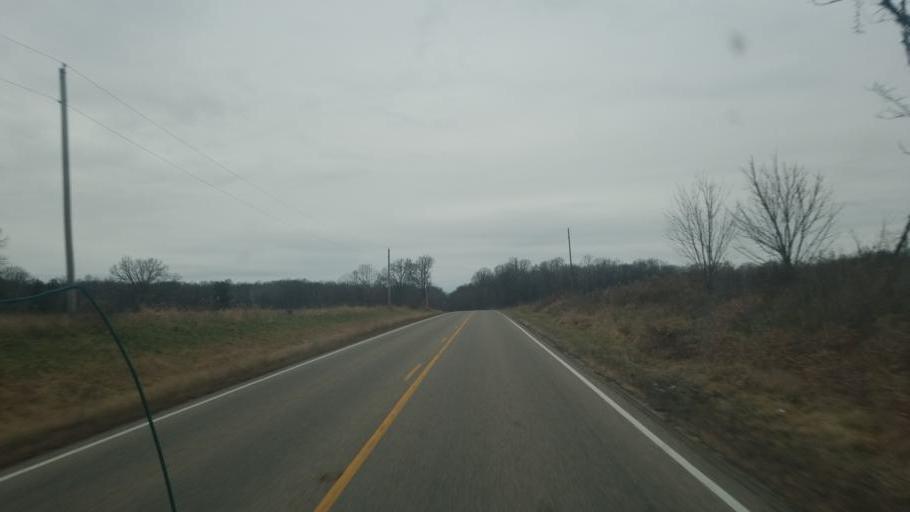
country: US
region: Indiana
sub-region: Clay County
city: Middlebury
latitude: 39.3623
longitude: -86.9569
